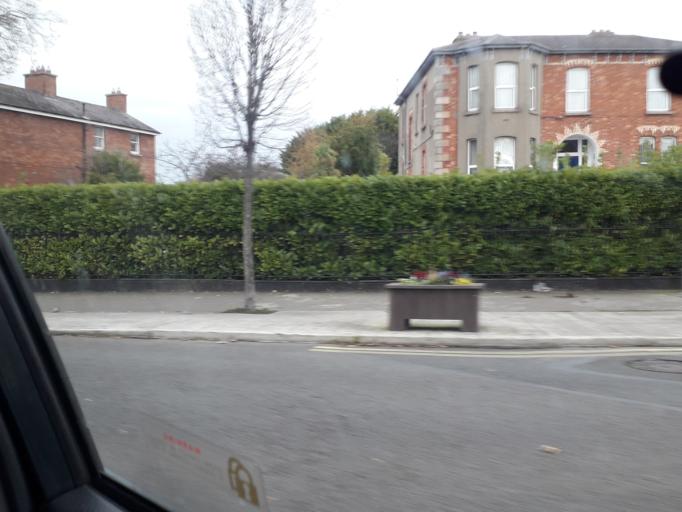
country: IE
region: Leinster
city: Sandymount
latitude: 53.3290
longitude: -6.2143
